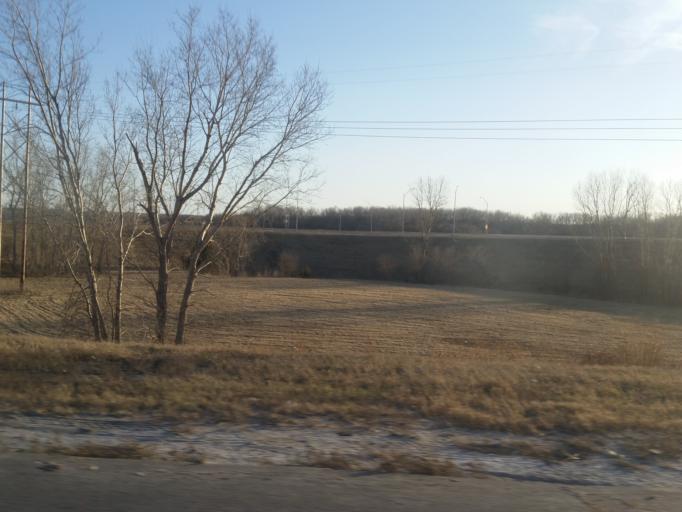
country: US
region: Nebraska
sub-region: Sarpy County
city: Offutt Air Force Base
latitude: 41.1399
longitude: -95.9348
